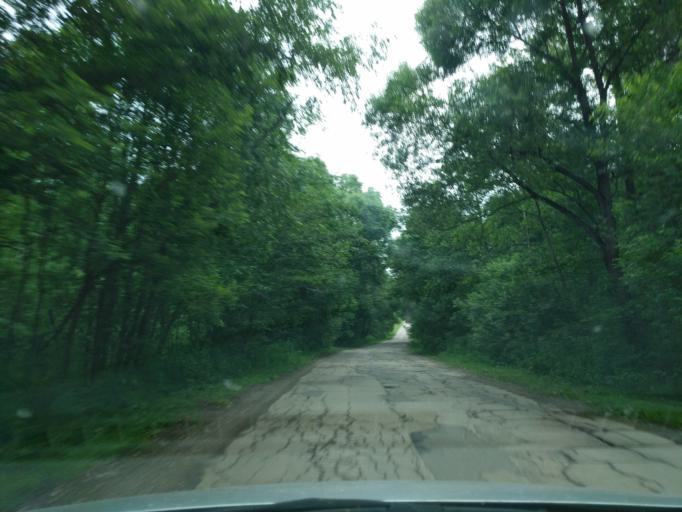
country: RU
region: Kaluga
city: Nikola-Lenivets
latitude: 54.7680
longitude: 35.7095
